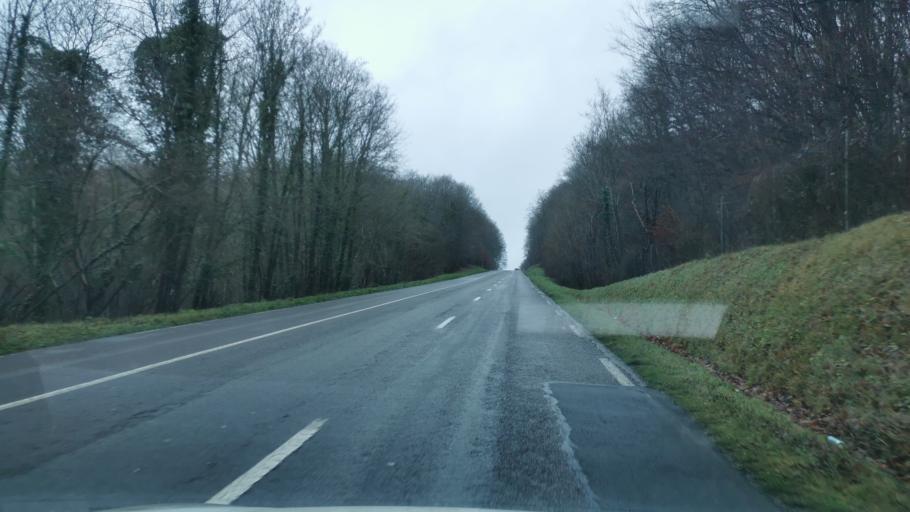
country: FR
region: Haute-Normandie
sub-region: Departement de l'Eure
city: Normanville
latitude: 49.0741
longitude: 1.1766
